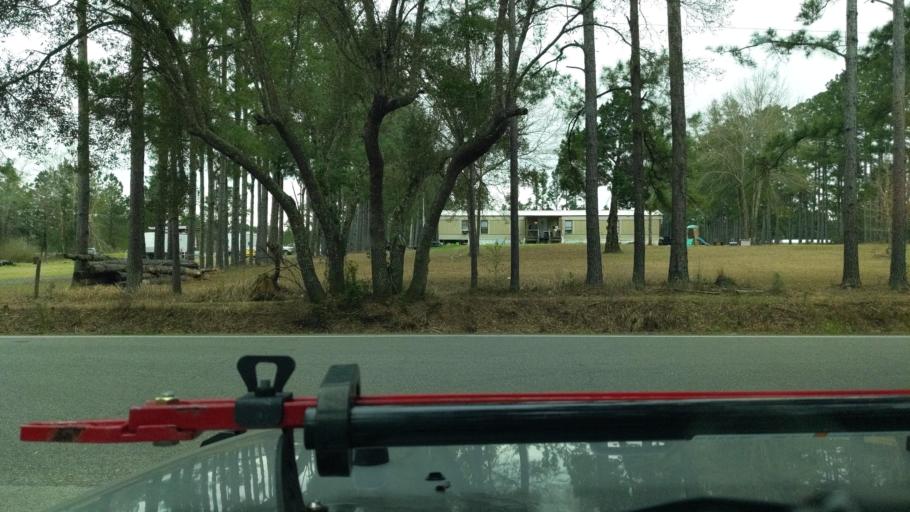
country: US
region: Alabama
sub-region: Baldwin County
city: Foley
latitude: 30.4580
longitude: -87.7792
